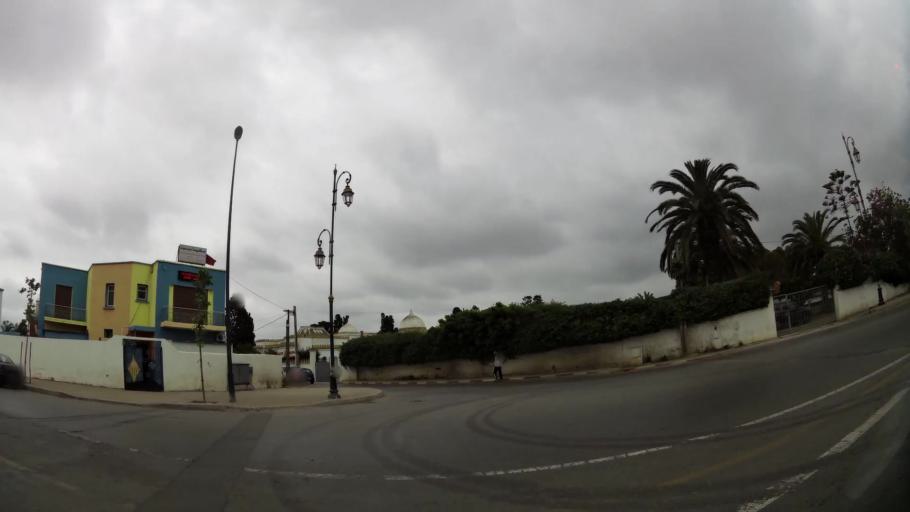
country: MA
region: Rabat-Sale-Zemmour-Zaer
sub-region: Rabat
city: Rabat
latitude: 33.9895
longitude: -6.8178
